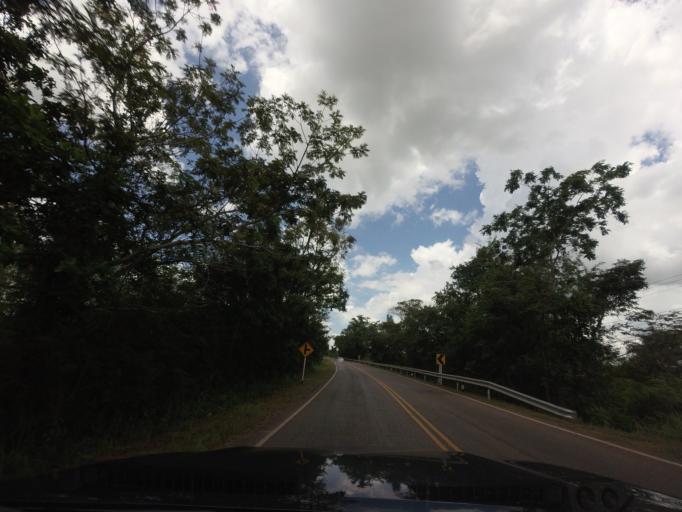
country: TH
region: Changwat Udon Thani
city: Phibun Rak
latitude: 17.6082
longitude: 103.0776
